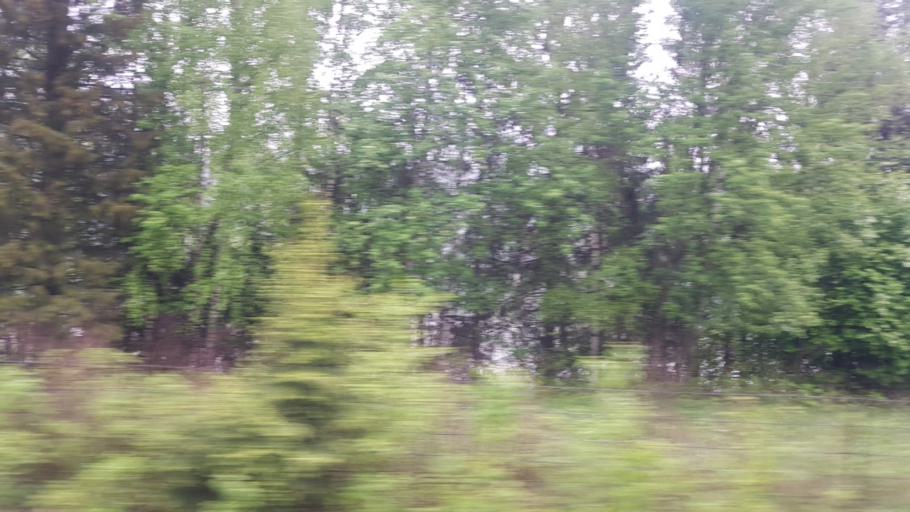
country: NO
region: Oppland
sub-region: Oyer
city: Tretten
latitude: 61.3910
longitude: 10.2538
